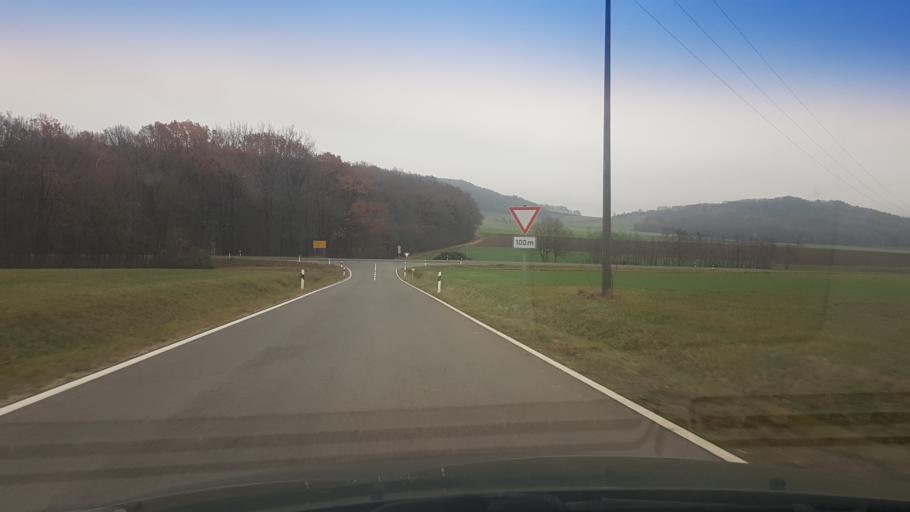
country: DE
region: Bavaria
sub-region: Upper Franconia
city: Schesslitz
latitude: 50.0147
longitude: 11.0092
